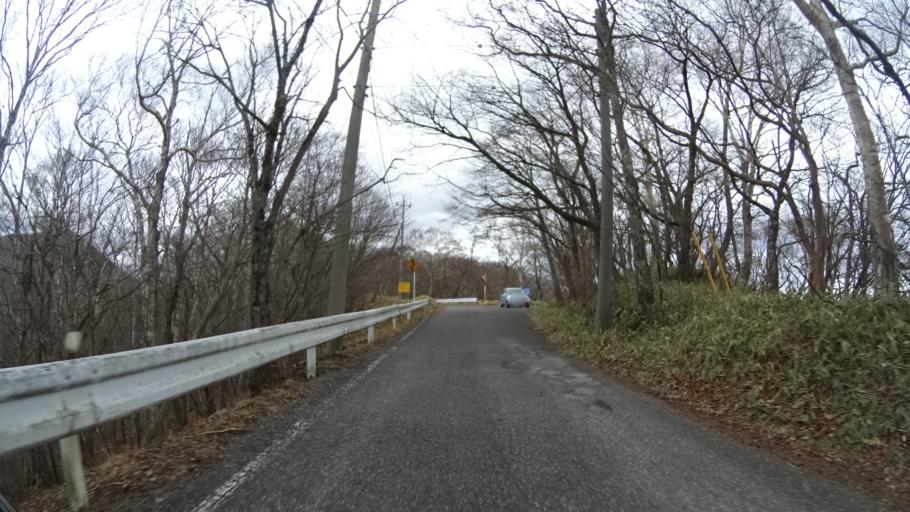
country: JP
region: Gunma
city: Omamacho-omama
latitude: 36.5254
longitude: 139.1764
